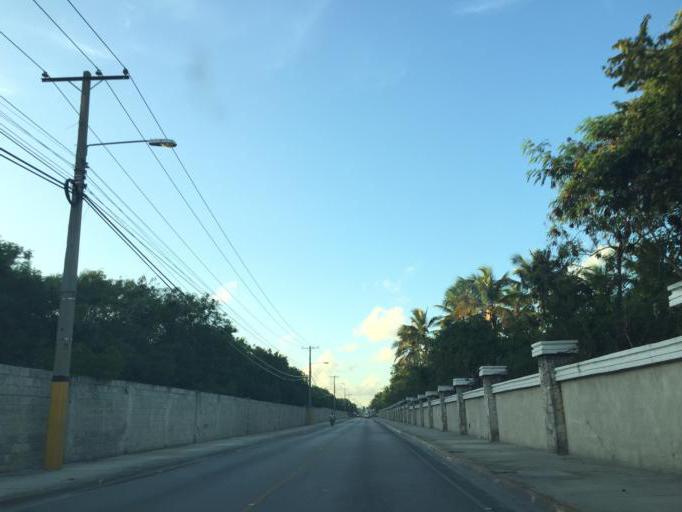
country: DO
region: San Juan
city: Punta Cana
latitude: 18.6875
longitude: -68.4322
